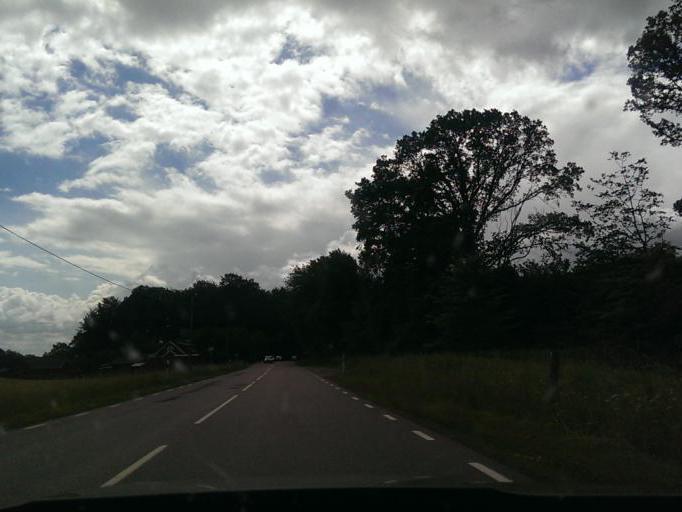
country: SE
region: Skane
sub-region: Klippans Kommun
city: Ljungbyhed
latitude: 56.0150
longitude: 13.2749
